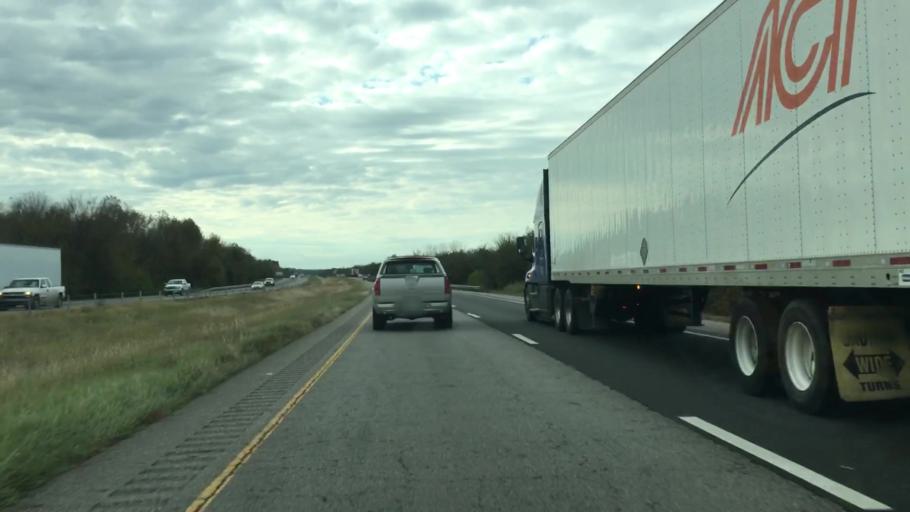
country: US
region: Arkansas
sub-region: Conway County
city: Morrilton
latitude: 35.1634
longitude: -92.6218
